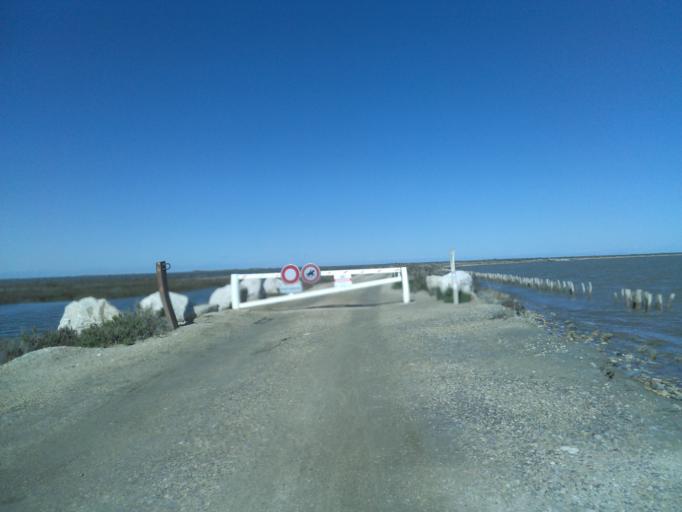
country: FR
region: Provence-Alpes-Cote d'Azur
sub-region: Departement des Bouches-du-Rhone
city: Saintes-Maries-de-la-Mer
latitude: 43.4183
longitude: 4.6216
